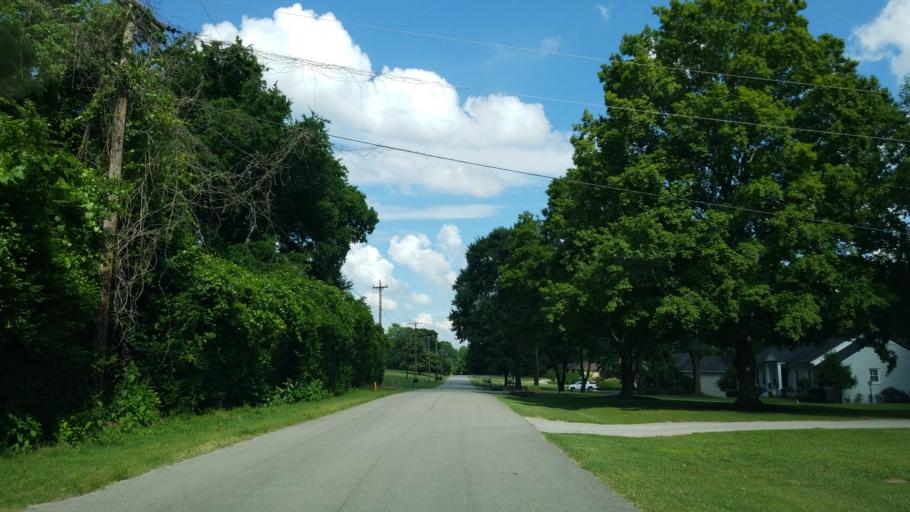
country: US
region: Tennessee
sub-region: Davidson County
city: Forest Hills
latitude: 36.0436
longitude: -86.8537
